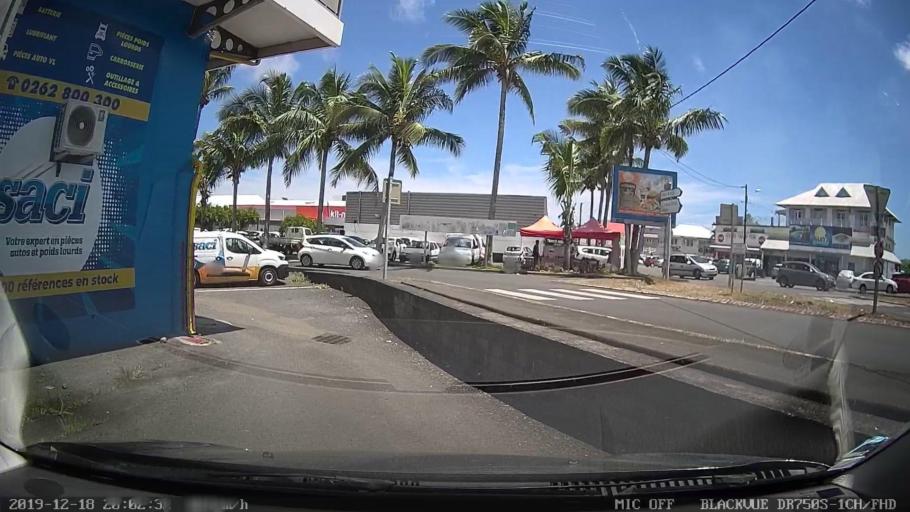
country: RE
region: Reunion
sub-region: Reunion
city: Saint-Andre
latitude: -20.9314
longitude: 55.6385
